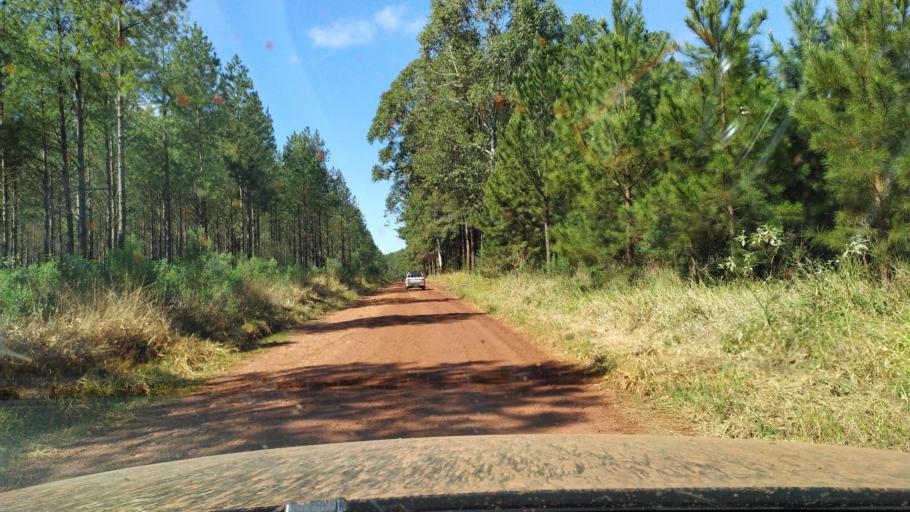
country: AR
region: Corrientes
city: Santo Tome
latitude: -28.3978
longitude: -56.0190
